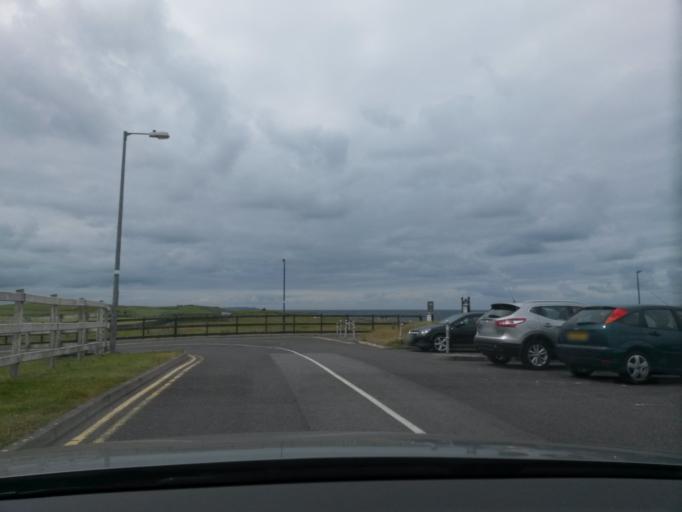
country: IE
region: Ulster
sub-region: County Donegal
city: Bundoran
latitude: 54.4900
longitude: -8.2689
